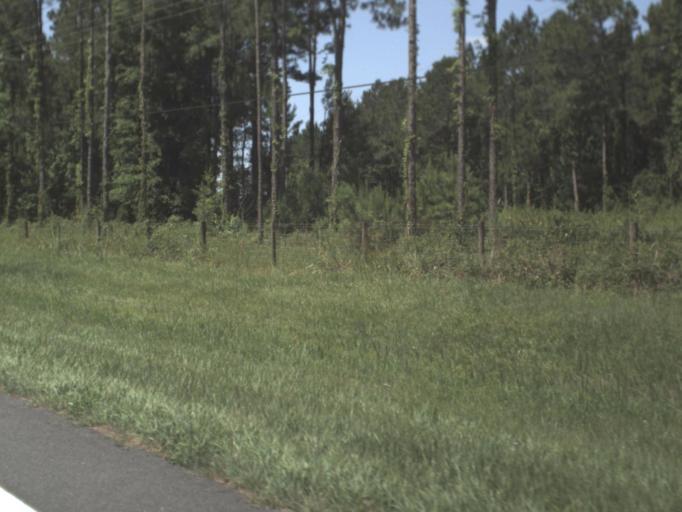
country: US
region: Florida
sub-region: Alachua County
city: Archer
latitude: 29.5051
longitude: -82.4065
